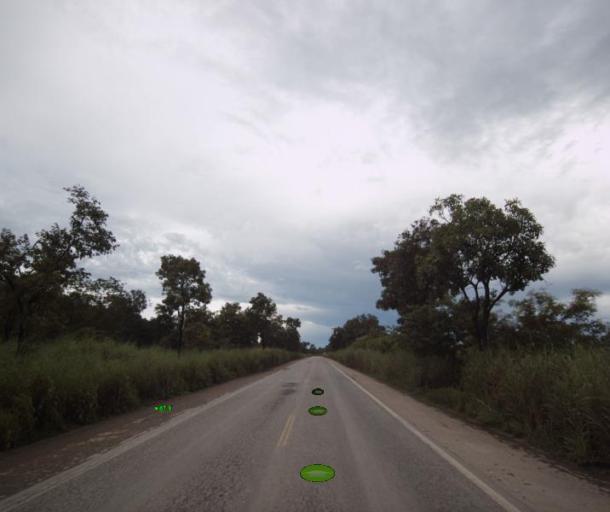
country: BR
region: Goias
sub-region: Porangatu
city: Porangatu
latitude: -13.5559
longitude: -49.0684
